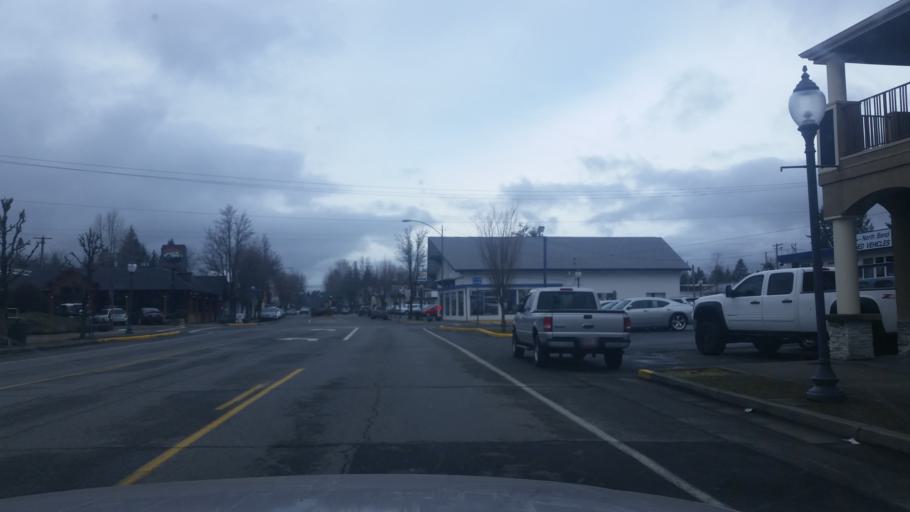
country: US
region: Washington
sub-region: King County
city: North Bend
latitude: 47.4940
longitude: -121.7839
